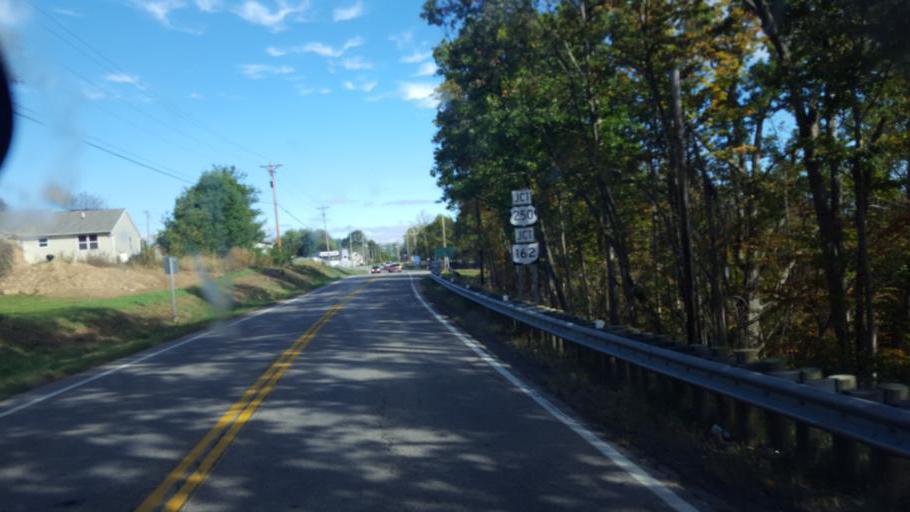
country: US
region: Ohio
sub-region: Huron County
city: Greenwich
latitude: 41.0926
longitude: -82.4885
